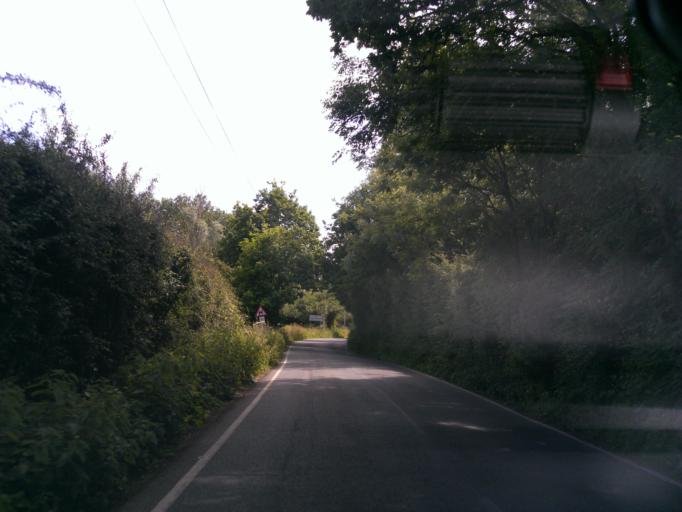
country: GB
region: England
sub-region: Essex
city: Hatfield Peverel
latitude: 51.7504
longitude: 0.5719
